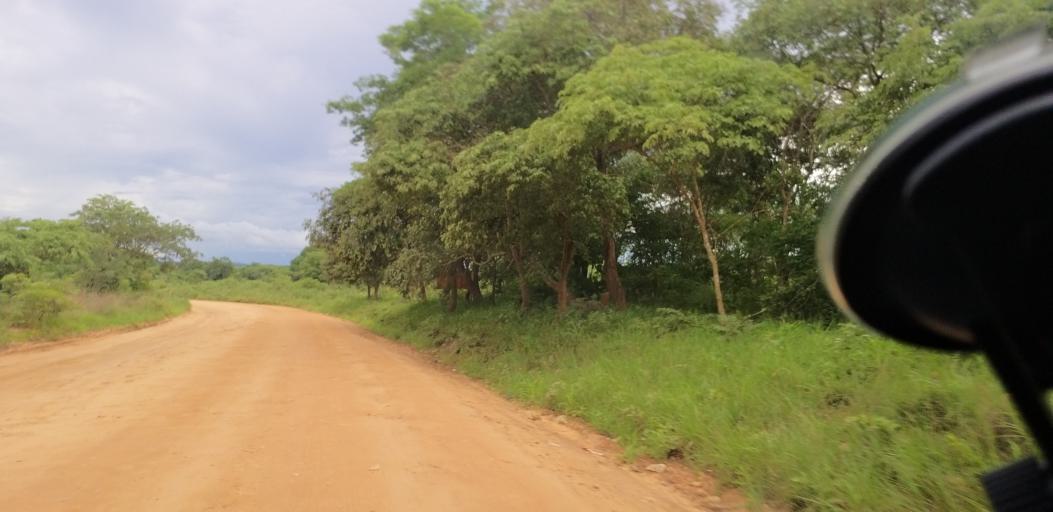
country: ZM
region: Lusaka
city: Chongwe
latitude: -15.1803
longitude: 28.4513
